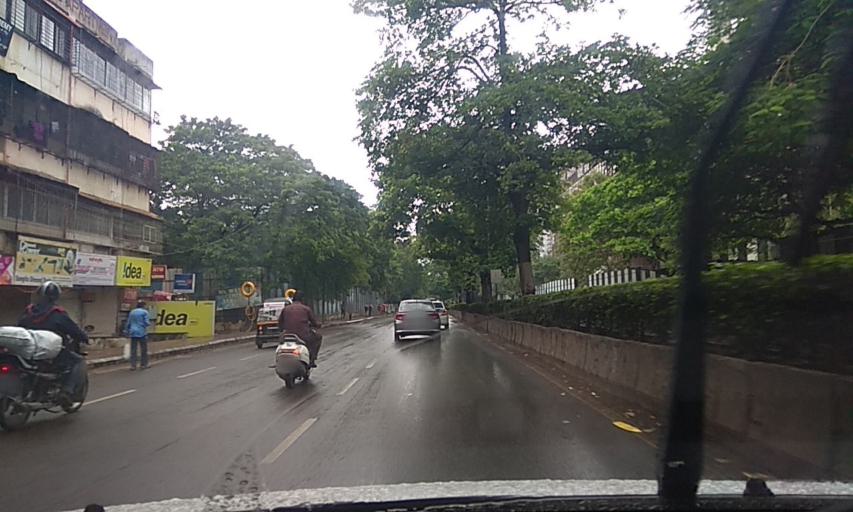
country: IN
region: Maharashtra
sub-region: Pune Division
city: Khadki
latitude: 18.5524
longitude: 73.8952
